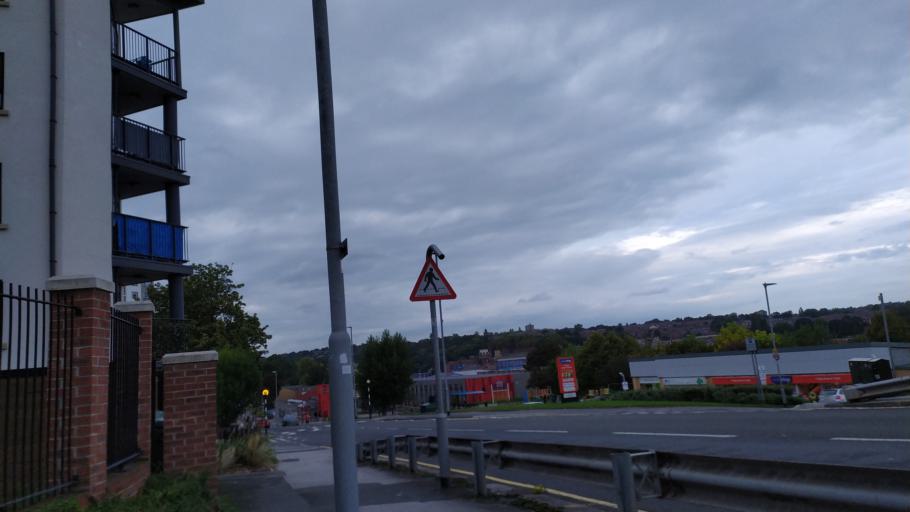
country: GB
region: England
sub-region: City and Borough of Leeds
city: Leeds
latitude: 53.8071
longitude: -1.5402
